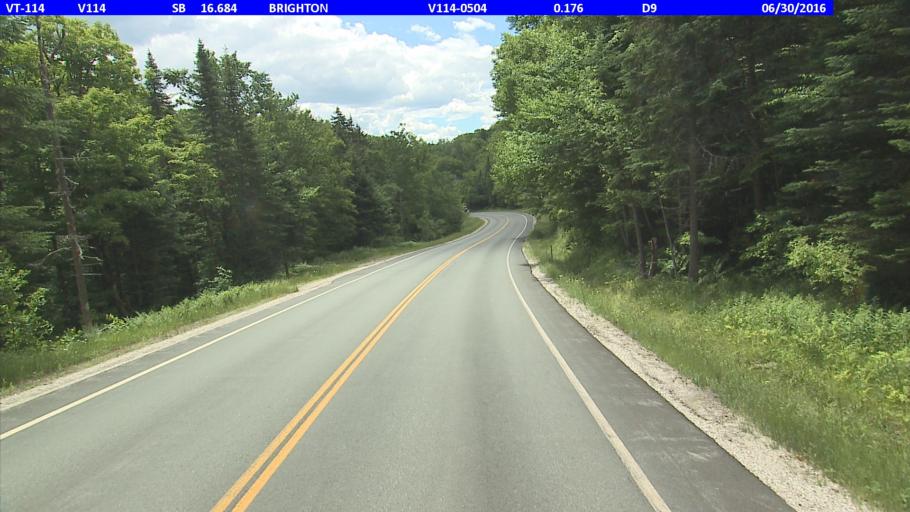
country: US
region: Vermont
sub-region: Caledonia County
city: Lyndonville
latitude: 44.7426
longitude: -71.8832
